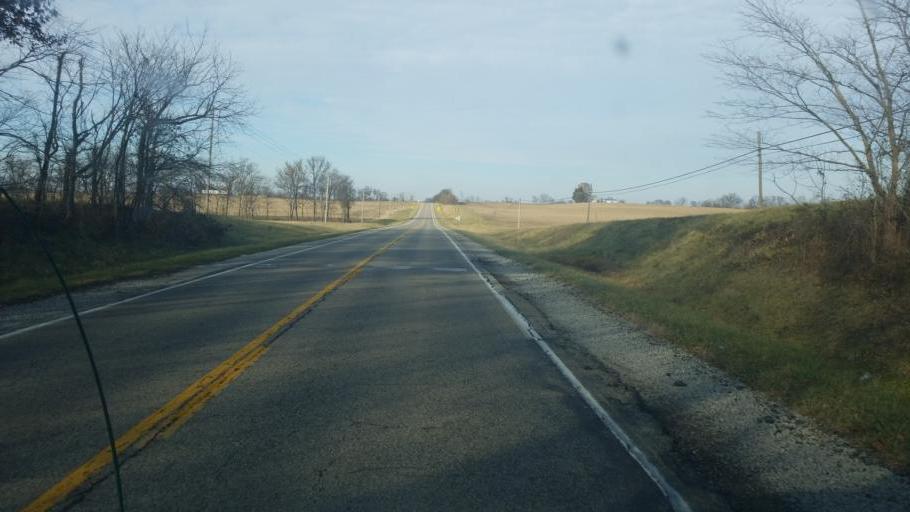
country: US
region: Illinois
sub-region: Lawrence County
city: Bridgeport
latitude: 38.6214
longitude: -87.6941
